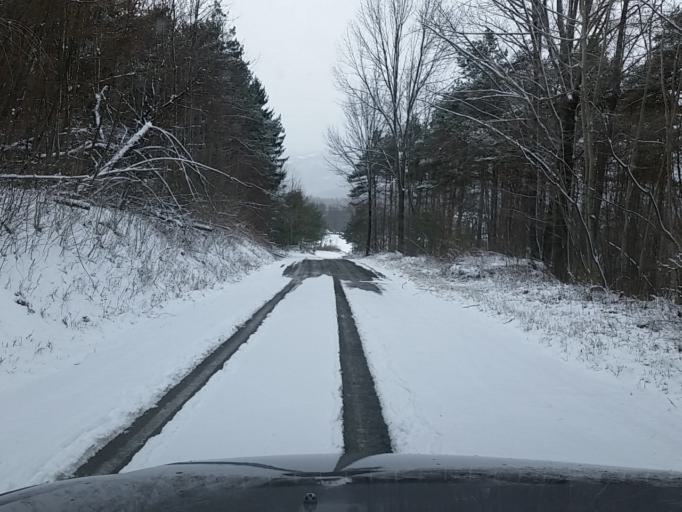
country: US
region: Pennsylvania
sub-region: Sullivan County
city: Laporte
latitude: 41.3592
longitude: -76.4743
